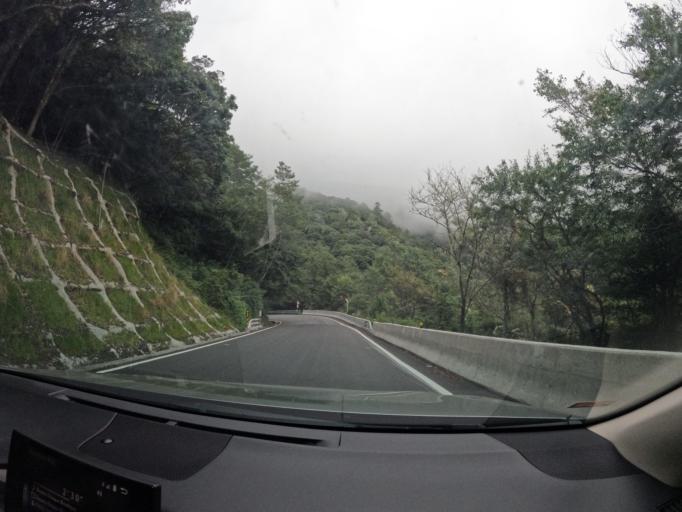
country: TW
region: Taiwan
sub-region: Taitung
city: Taitung
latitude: 23.2446
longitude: 120.9911
